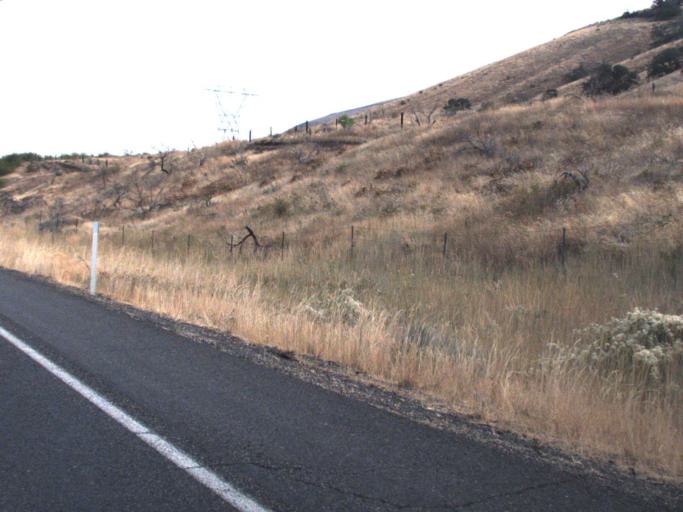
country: US
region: Washington
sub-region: Klickitat County
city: Goldendale
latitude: 46.0765
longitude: -120.5558
